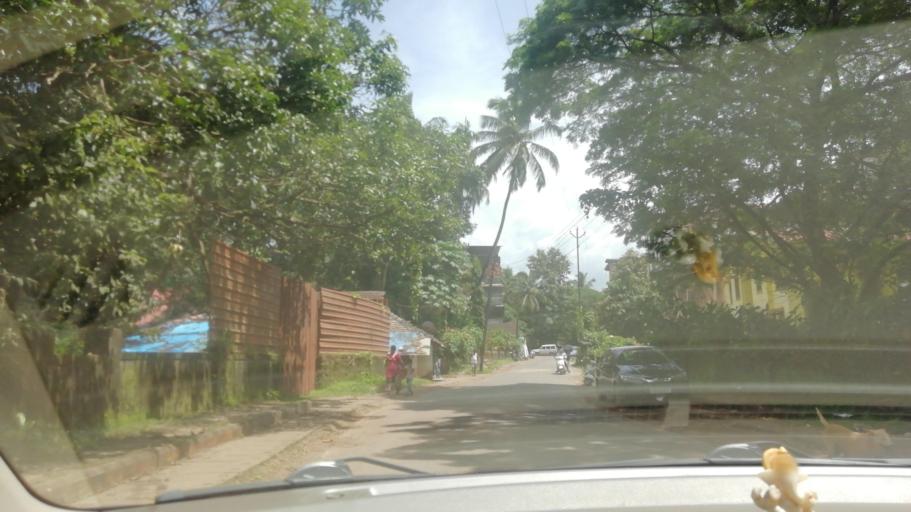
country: IN
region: Goa
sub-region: North Goa
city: Queula
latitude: 15.3947
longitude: 74.0007
